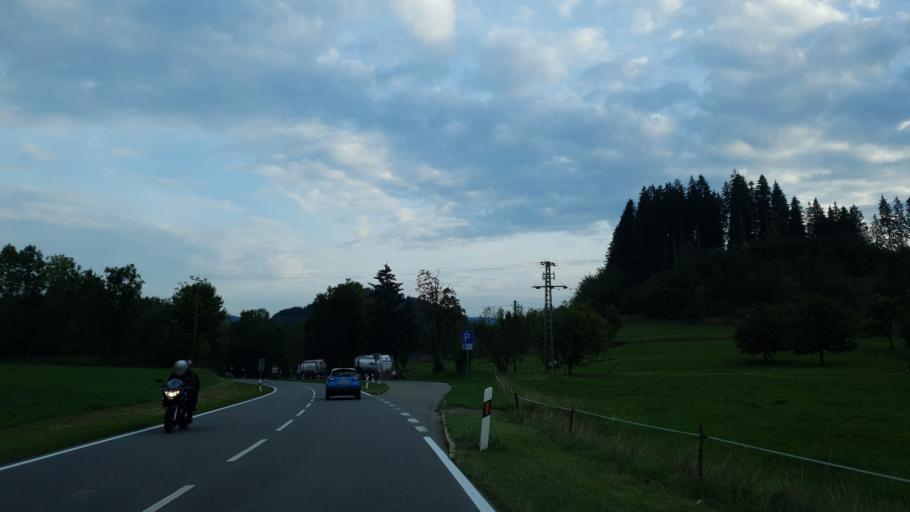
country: DE
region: Baden-Wuerttemberg
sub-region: Tuebingen Region
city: Isny im Allgau
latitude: 47.6838
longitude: 10.0786
